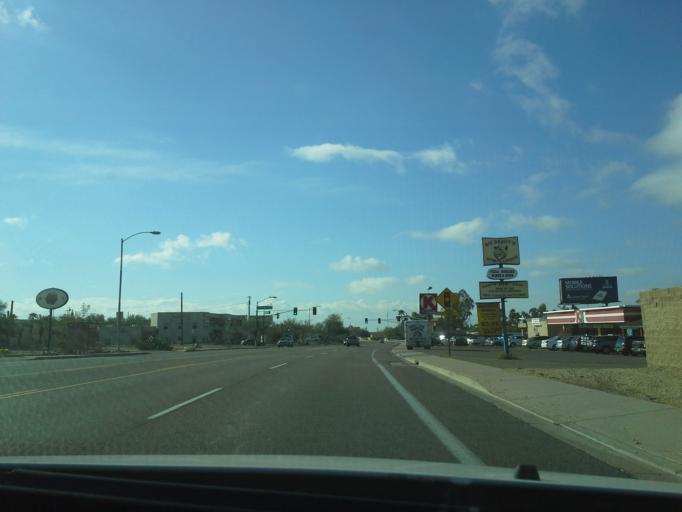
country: US
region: Arizona
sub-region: Maricopa County
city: Paradise Valley
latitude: 33.5834
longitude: -112.0511
